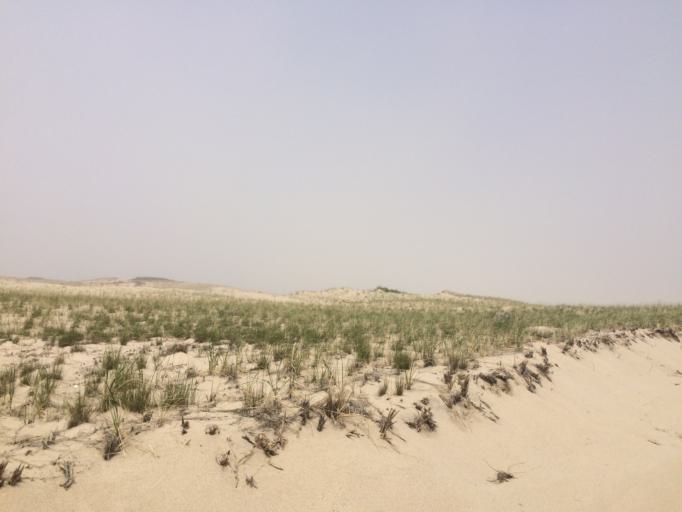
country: US
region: Massachusetts
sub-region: Barnstable County
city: Provincetown
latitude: 42.0703
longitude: -70.2379
